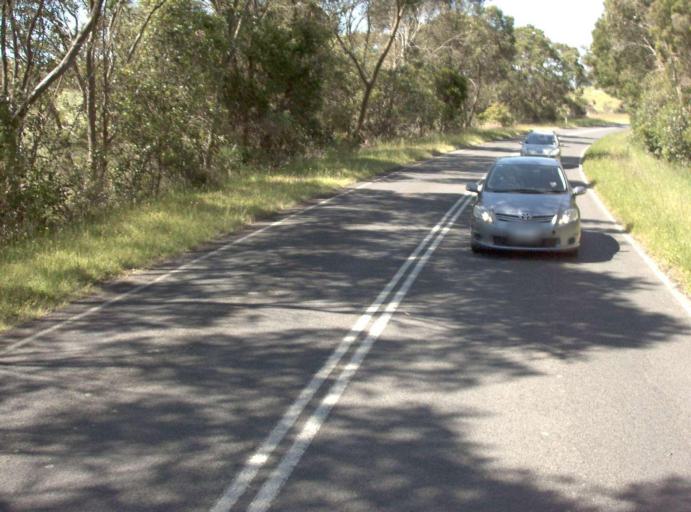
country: AU
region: Victoria
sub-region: Bass Coast
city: North Wonthaggi
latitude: -38.7466
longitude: 146.1370
